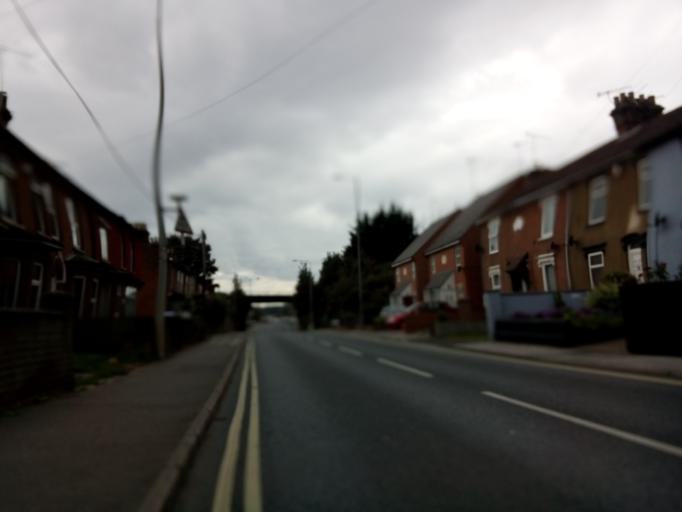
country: GB
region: England
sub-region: Suffolk
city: Ipswich
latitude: 52.0439
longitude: 1.1536
